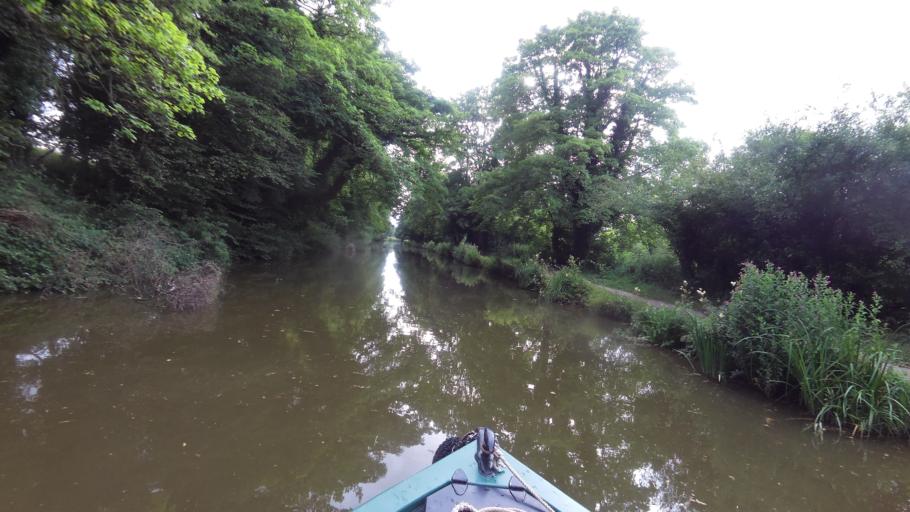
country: GB
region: England
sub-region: West Berkshire
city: Kintbury
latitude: 51.4025
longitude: -1.4365
